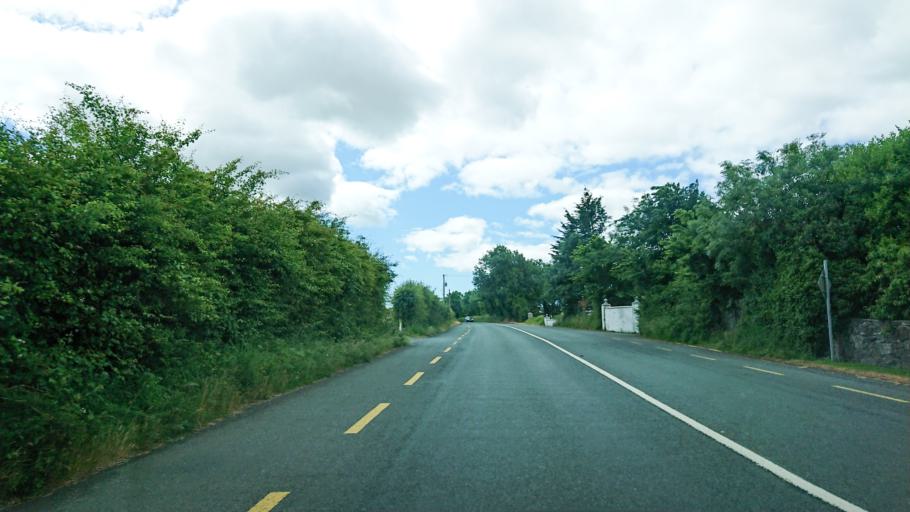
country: IE
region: Munster
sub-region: Waterford
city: Tra Mhor
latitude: 52.2217
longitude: -7.1987
